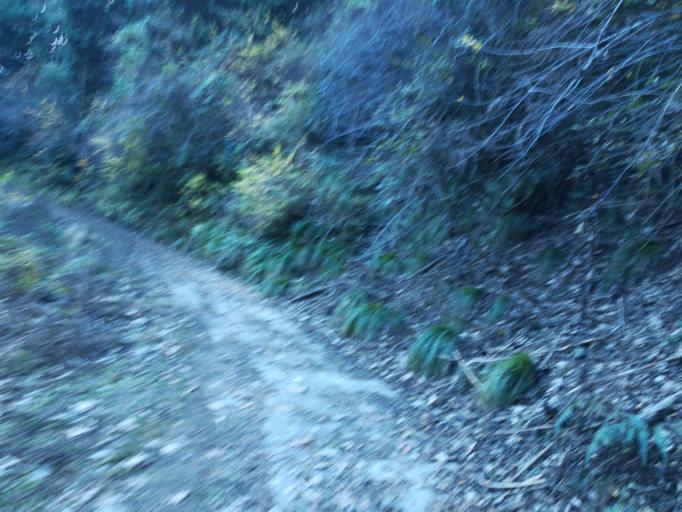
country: JP
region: Kyoto
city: Kameoka
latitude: 34.9847
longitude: 135.6272
